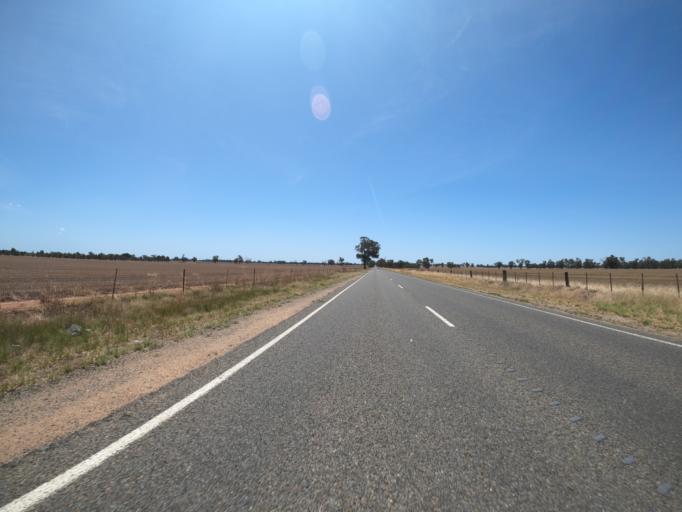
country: AU
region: Victoria
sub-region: Moira
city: Yarrawonga
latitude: -36.0759
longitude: 145.9954
